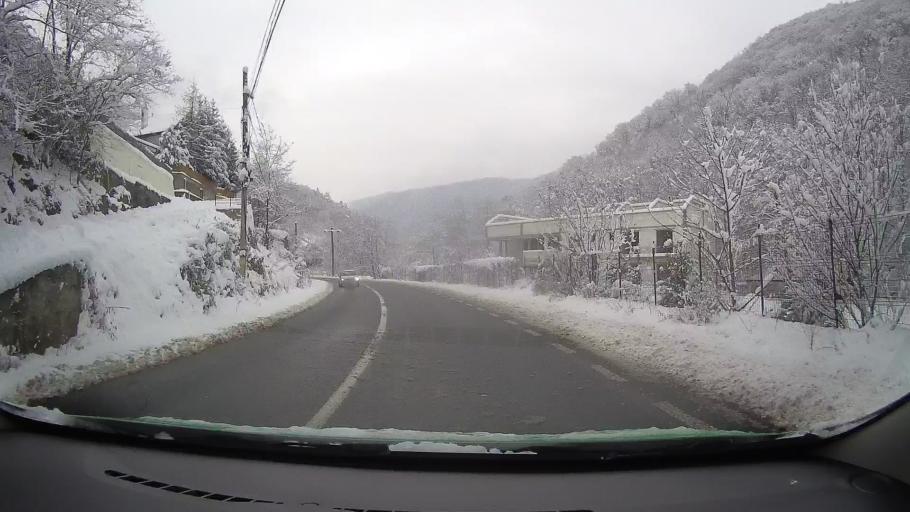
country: RO
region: Alba
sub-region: Comuna Sugag
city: Sugag
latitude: 45.7902
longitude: 23.6079
